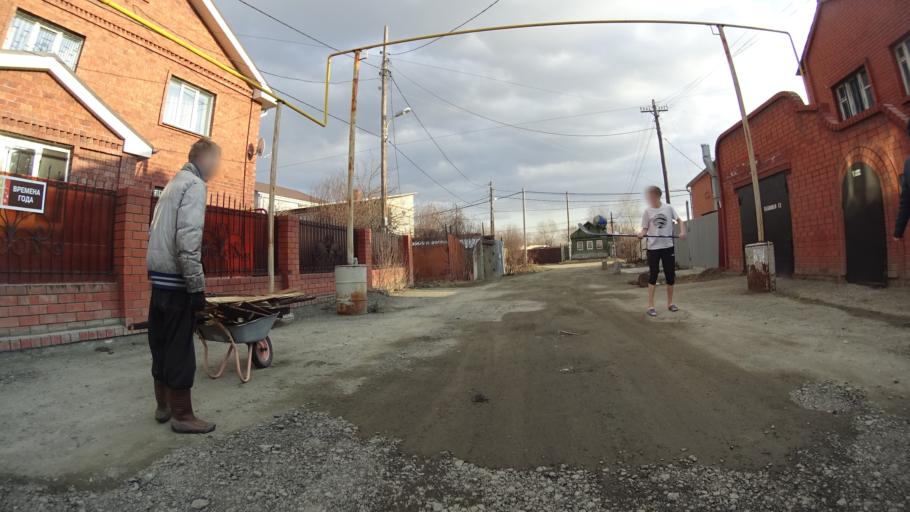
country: RU
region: Chelyabinsk
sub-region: Gorod Chelyabinsk
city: Chelyabinsk
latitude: 55.1344
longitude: 61.3920
